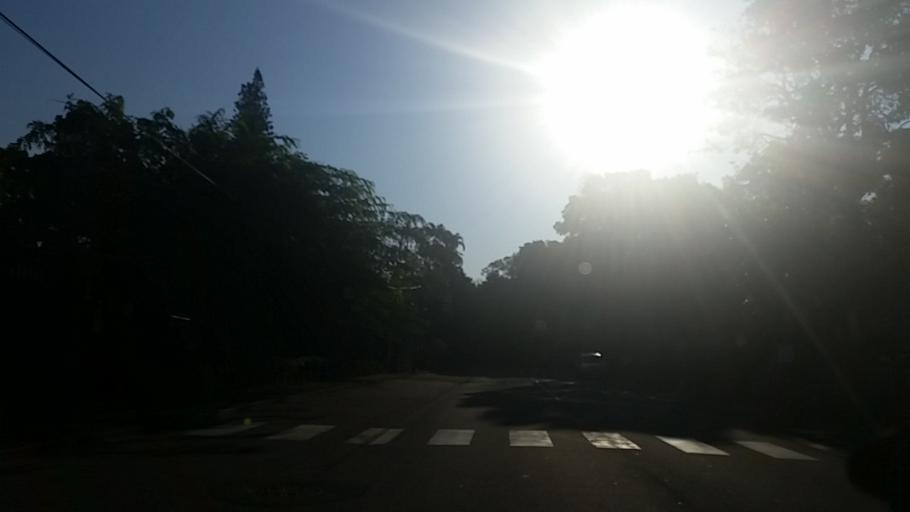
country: ZA
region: KwaZulu-Natal
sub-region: eThekwini Metropolitan Municipality
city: Berea
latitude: -29.8391
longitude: 30.9206
